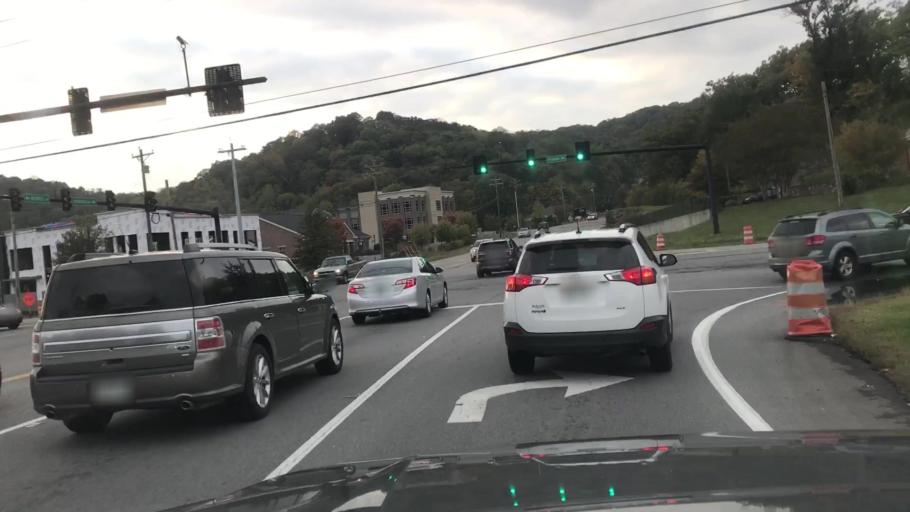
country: US
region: Tennessee
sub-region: Williamson County
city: Franklin
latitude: 35.9733
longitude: -86.8326
